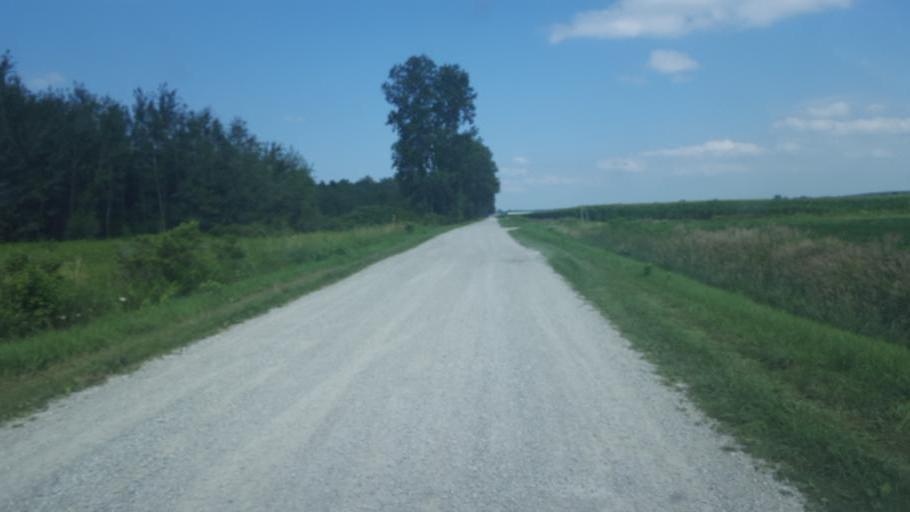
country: US
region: Ohio
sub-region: Huron County
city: Willard
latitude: 40.9959
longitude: -82.7635
